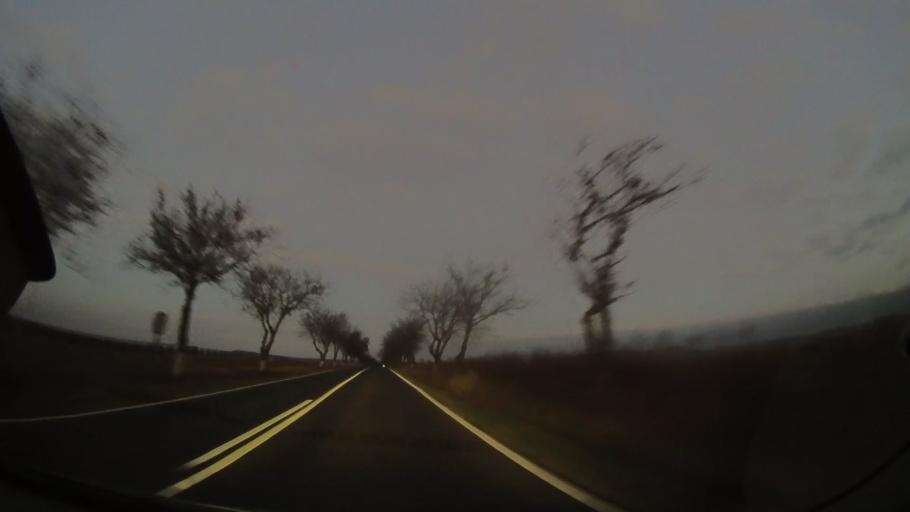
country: RO
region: Tulcea
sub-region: Comuna Frecatei
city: Cataloi
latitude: 45.0834
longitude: 28.7018
